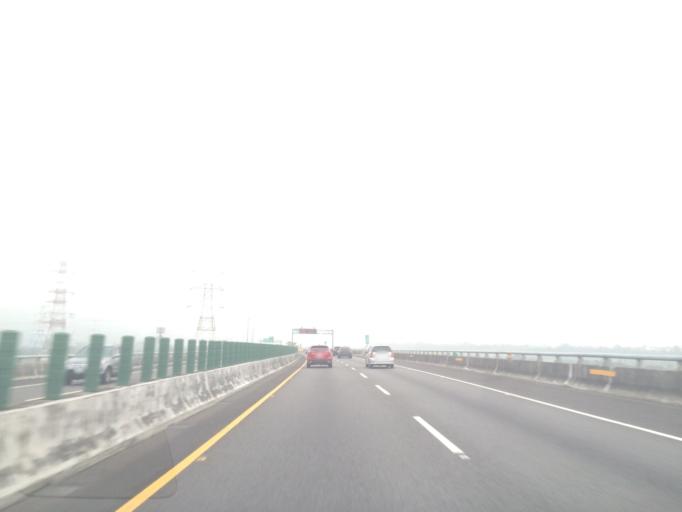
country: TW
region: Taiwan
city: Zhongxing New Village
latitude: 24.0071
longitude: 120.7093
